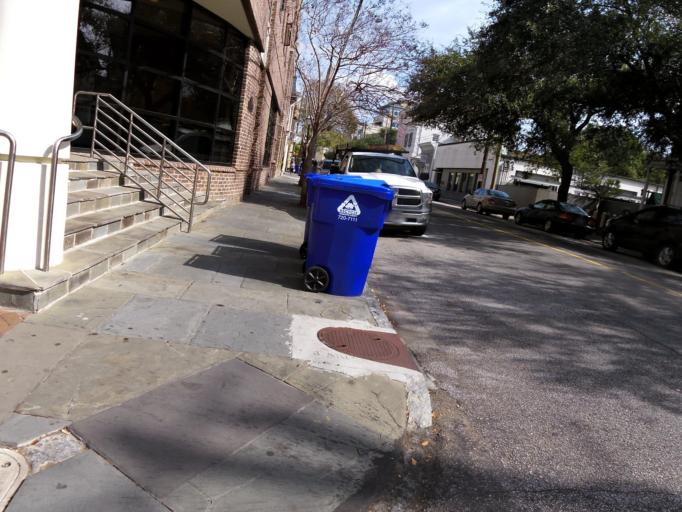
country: US
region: South Carolina
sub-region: Charleston County
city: Charleston
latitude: 32.7817
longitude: -79.9362
